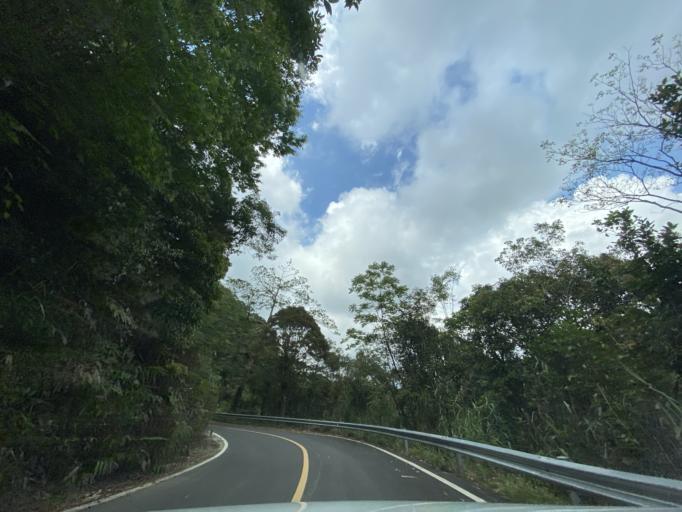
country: CN
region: Hainan
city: Diaoluoshan
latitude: 18.7002
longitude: 109.8832
